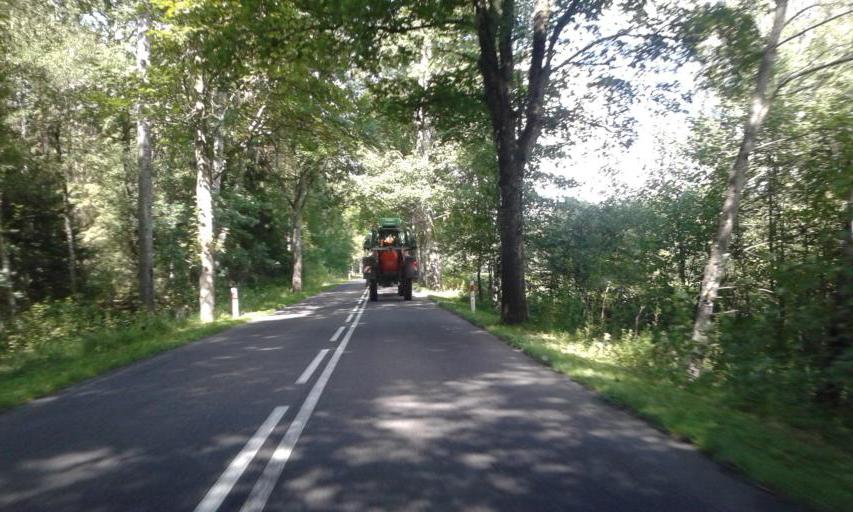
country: PL
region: West Pomeranian Voivodeship
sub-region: Powiat slawienski
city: Slawno
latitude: 54.2437
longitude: 16.7072
